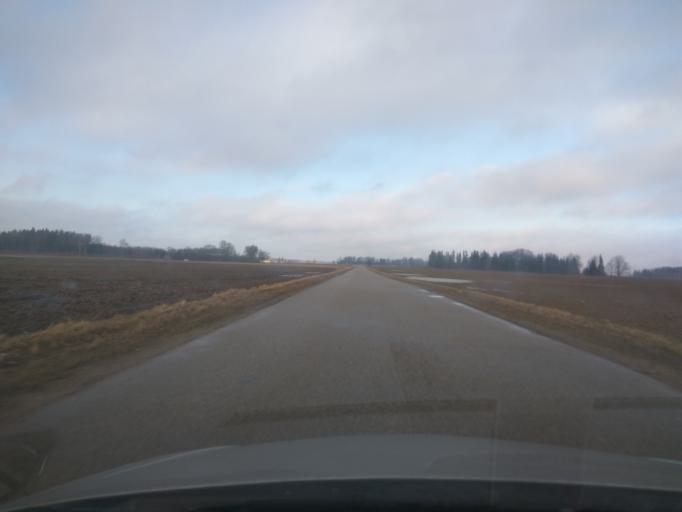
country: LV
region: Saldus Rajons
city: Saldus
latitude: 56.7872
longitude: 22.3875
